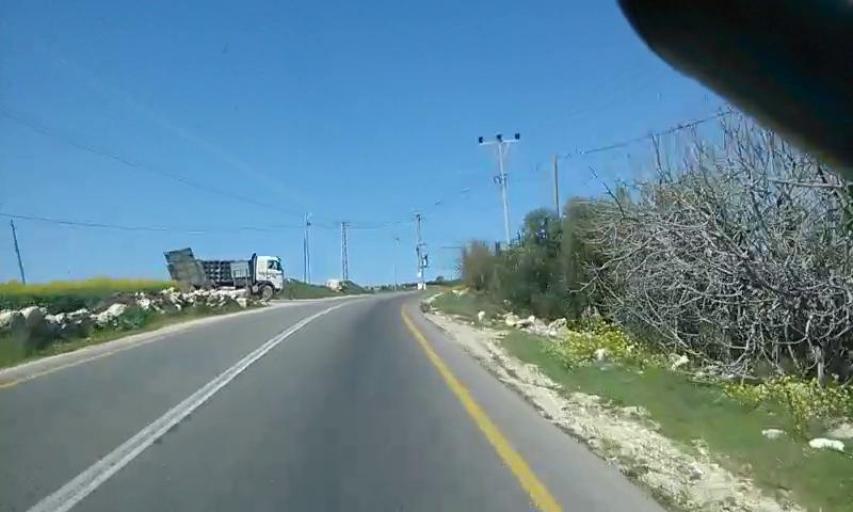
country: PS
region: West Bank
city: Marah Rabbah
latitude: 31.6451
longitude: 35.1918
